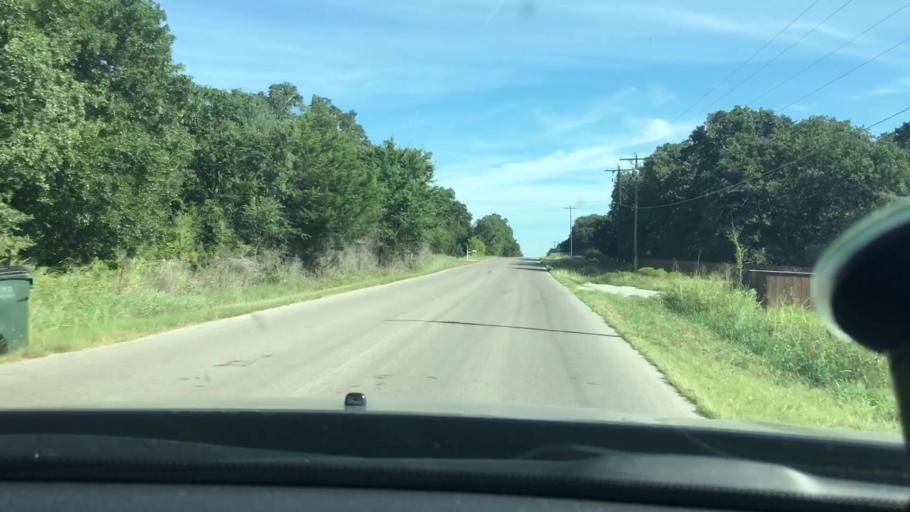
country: US
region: Oklahoma
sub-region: Carter County
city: Lone Grove
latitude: 34.2349
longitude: -97.2474
